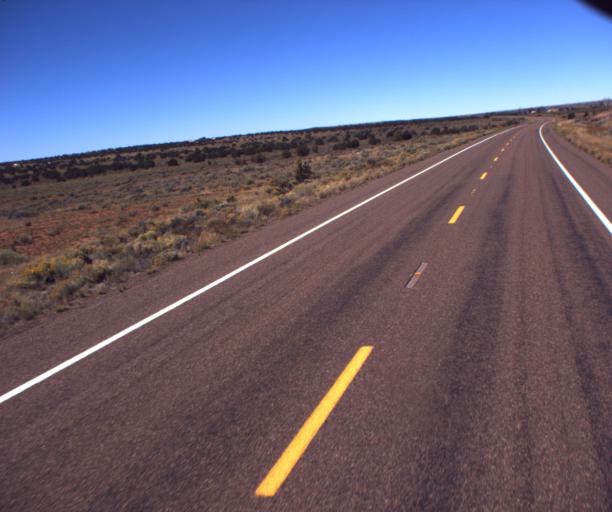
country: US
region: Arizona
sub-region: Apache County
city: Saint Johns
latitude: 34.6068
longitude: -109.6465
